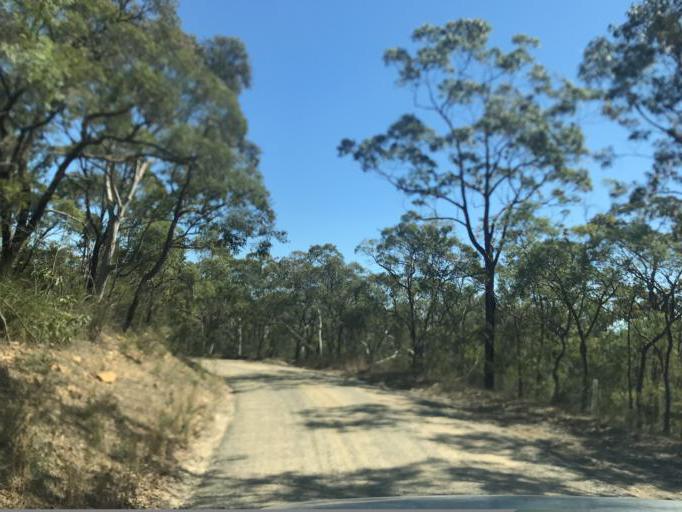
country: AU
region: New South Wales
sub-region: Wyong Shire
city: Little Jilliby
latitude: -33.1458
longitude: 151.0860
